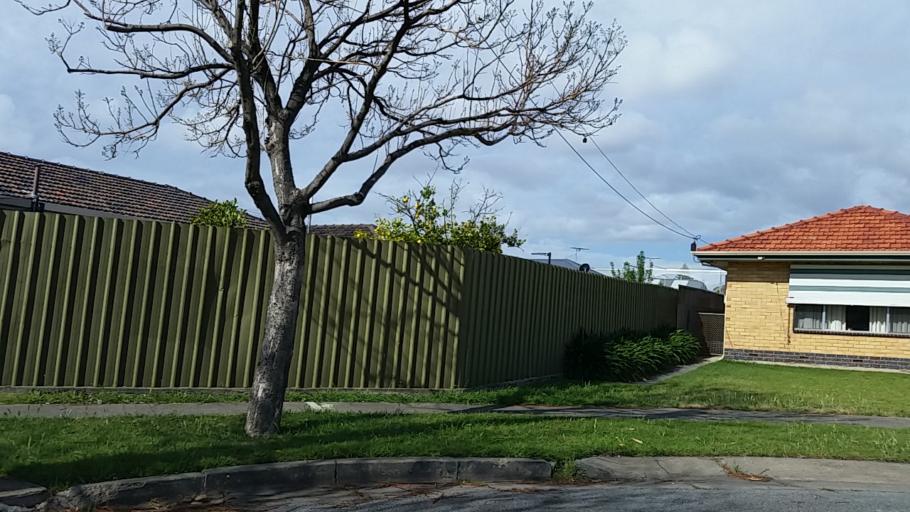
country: AU
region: South Australia
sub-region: Charles Sturt
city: Royal Park
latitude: -34.8852
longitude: 138.5092
